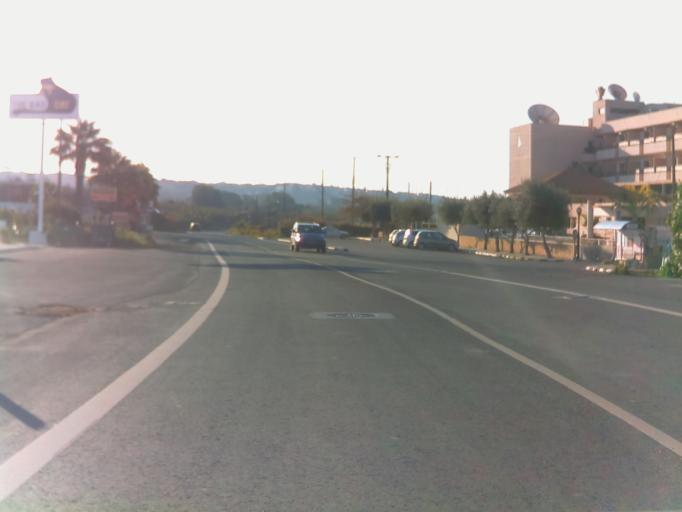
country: CY
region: Pafos
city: Kissonerga
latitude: 34.8226
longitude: 32.3927
